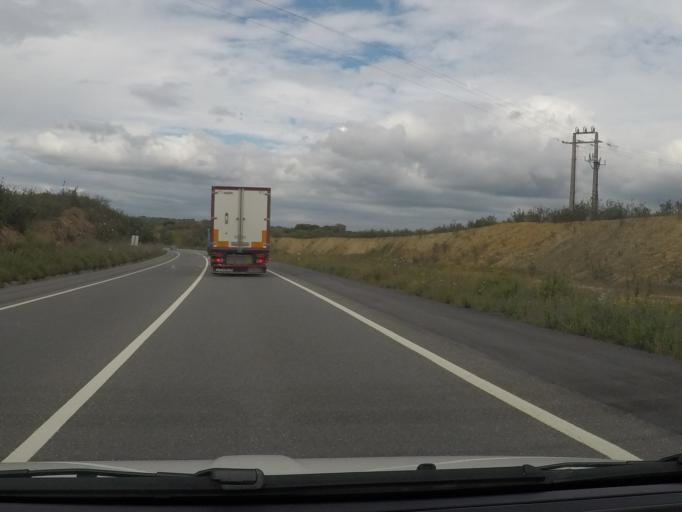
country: PT
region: Setubal
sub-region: Santiago do Cacem
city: Santiago do Cacem
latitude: 38.0746
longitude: -8.6464
